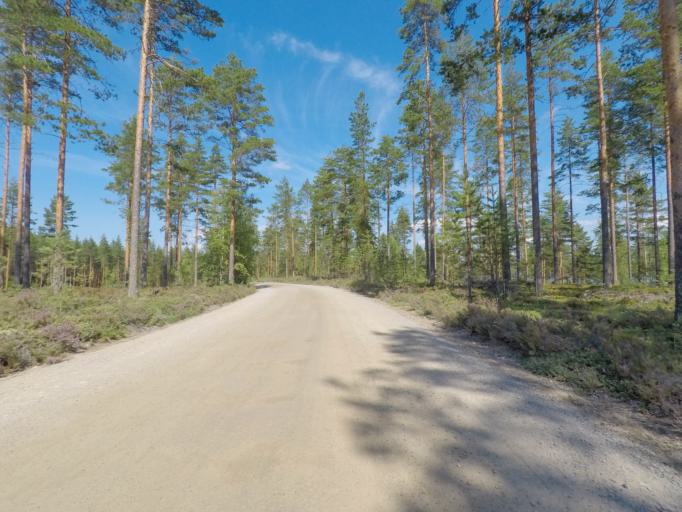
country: FI
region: Southern Savonia
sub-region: Mikkeli
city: Puumala
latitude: 61.4194
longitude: 28.0426
